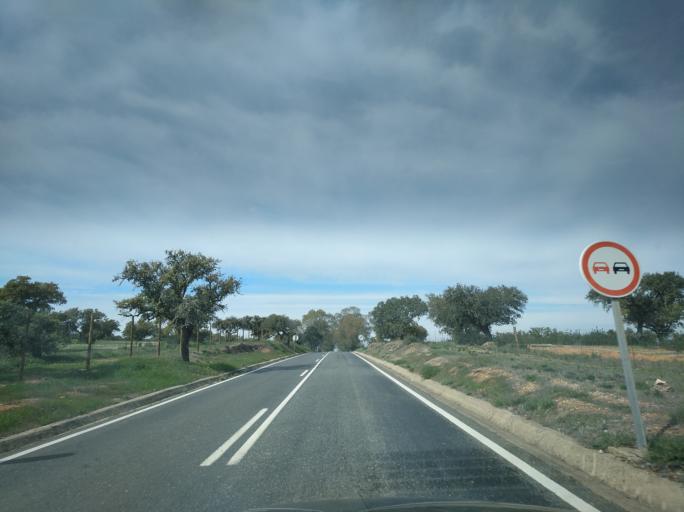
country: PT
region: Beja
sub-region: Mertola
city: Mertola
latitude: 37.7321
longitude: -7.7693
